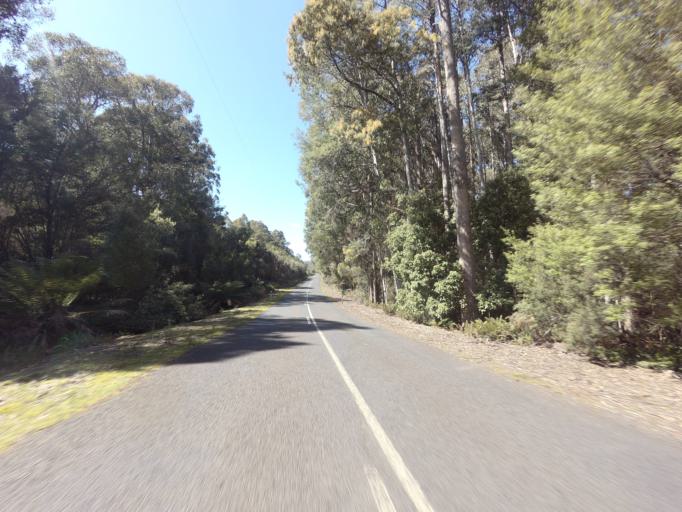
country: AU
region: Tasmania
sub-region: Derwent Valley
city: New Norfolk
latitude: -42.7655
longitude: 146.5541
